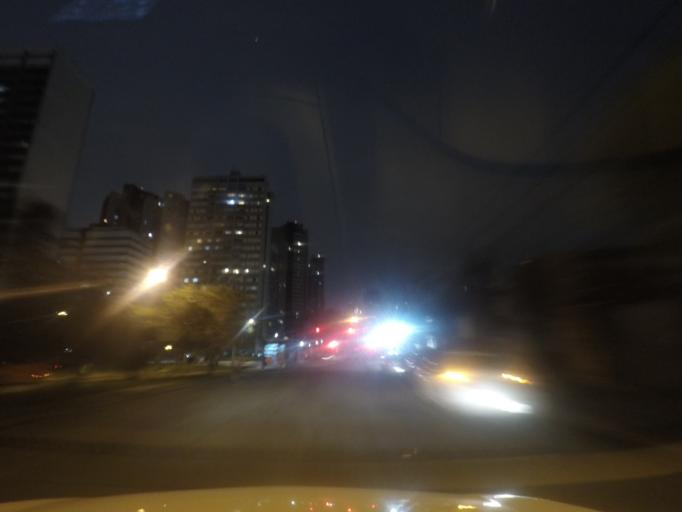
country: BR
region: Parana
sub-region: Curitiba
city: Curitiba
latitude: -25.4284
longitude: -49.2879
